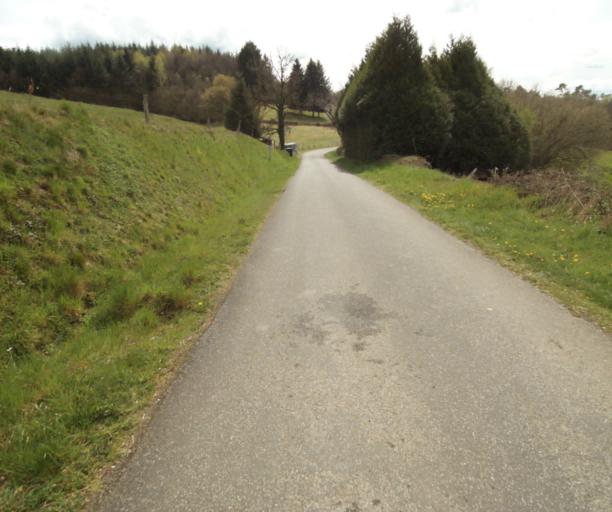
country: FR
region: Limousin
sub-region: Departement de la Correze
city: Laguenne
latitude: 45.2190
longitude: 1.8671
